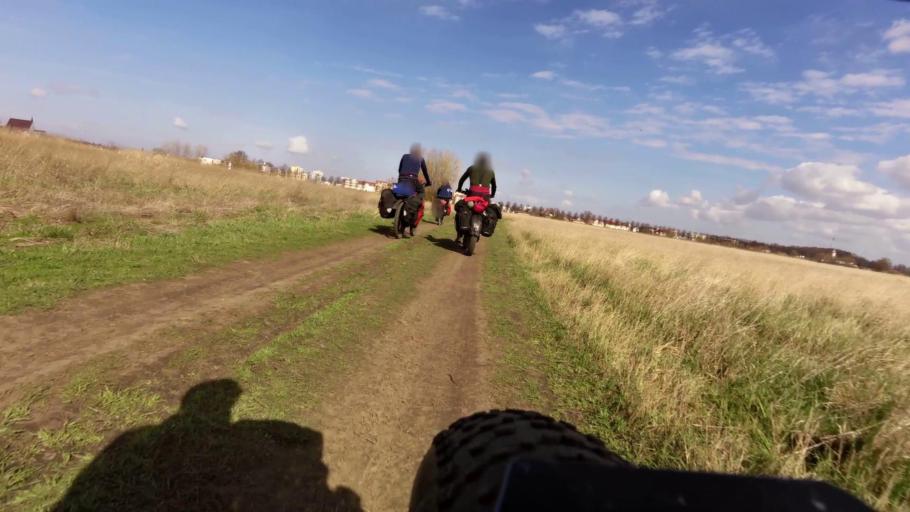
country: PL
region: Lubusz
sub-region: Powiat slubicki
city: Slubice
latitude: 52.3414
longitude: 14.5642
